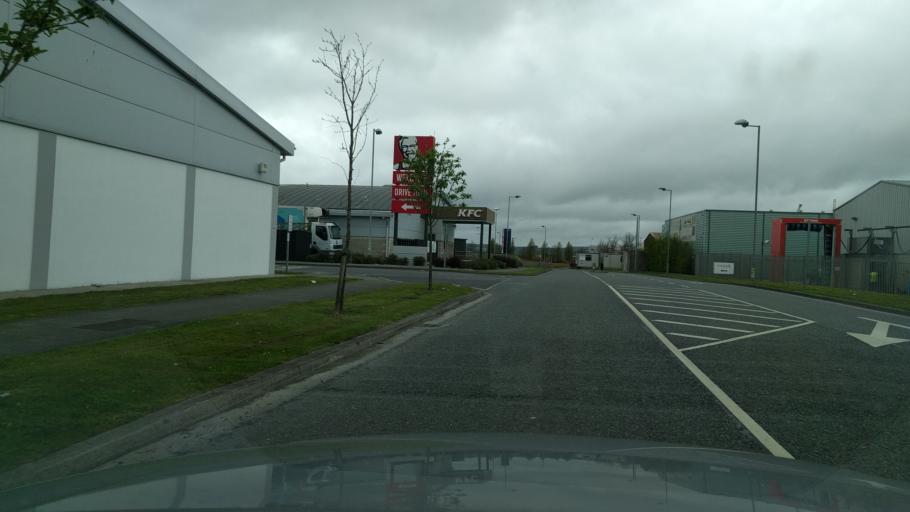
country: IE
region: Leinster
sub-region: Lu
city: Drogheda
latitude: 53.7023
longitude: -6.3769
